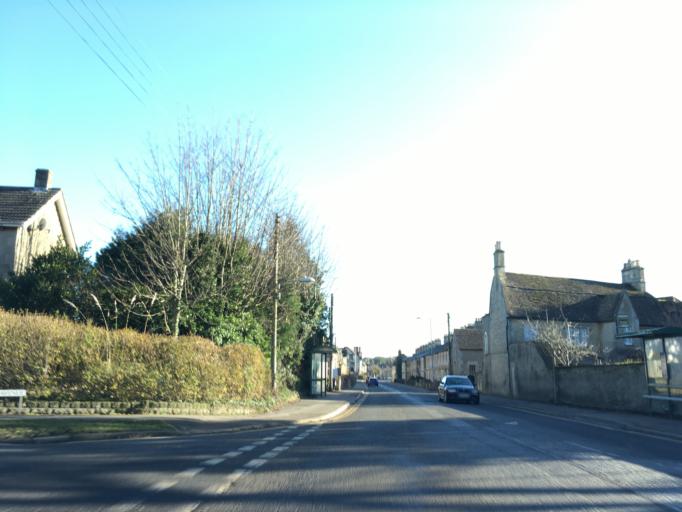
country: GB
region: England
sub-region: Wiltshire
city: Chippenham
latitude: 51.4635
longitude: -2.1264
